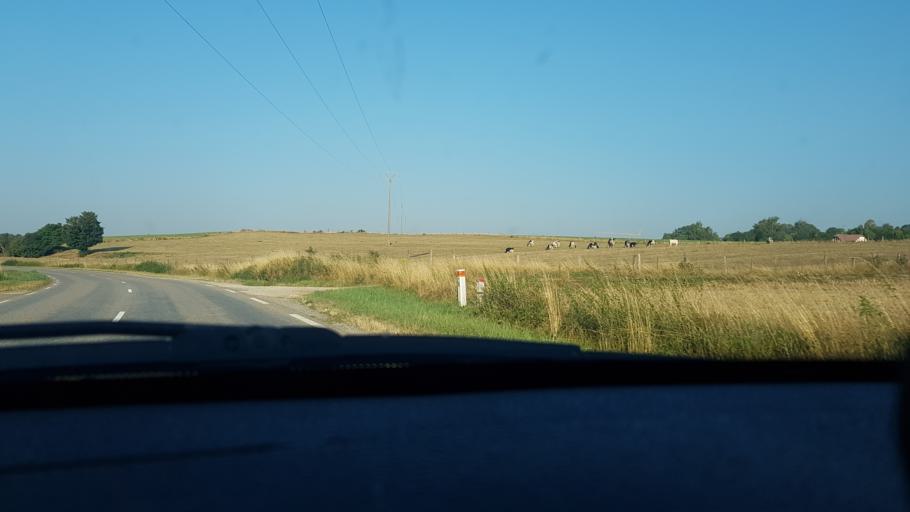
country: FR
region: Lorraine
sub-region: Departement des Vosges
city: Charmes
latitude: 48.3663
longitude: 6.2687
